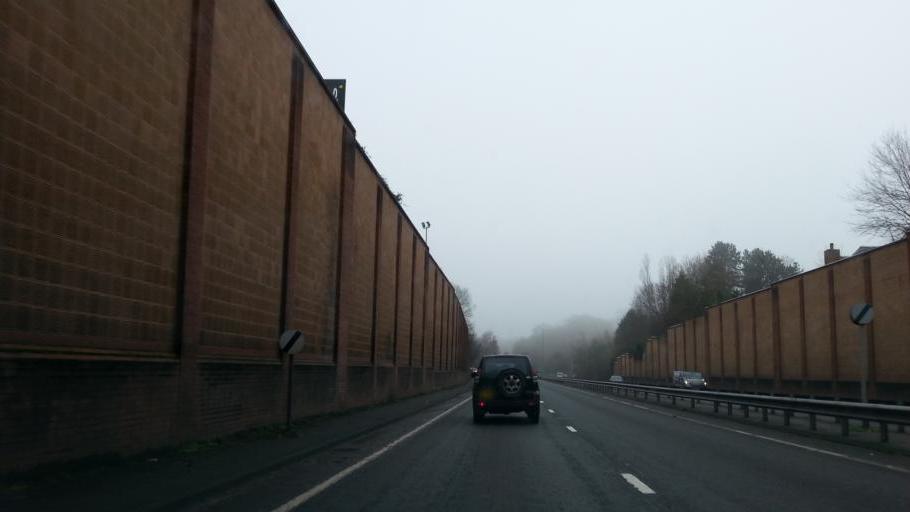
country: GB
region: England
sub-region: Cheshire East
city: Wilmslow
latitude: 53.3260
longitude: -2.2251
